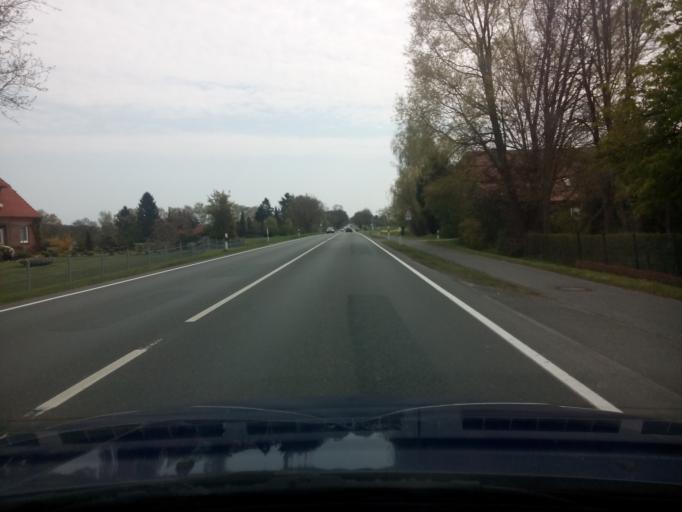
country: DE
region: Lower Saxony
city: Sustedt
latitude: 52.8661
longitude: 8.8764
